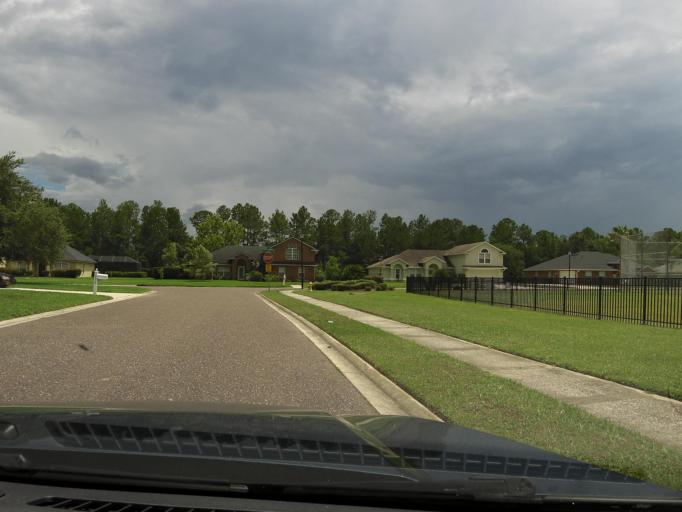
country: US
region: Florida
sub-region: Duval County
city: Jacksonville
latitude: 30.4240
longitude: -81.7257
